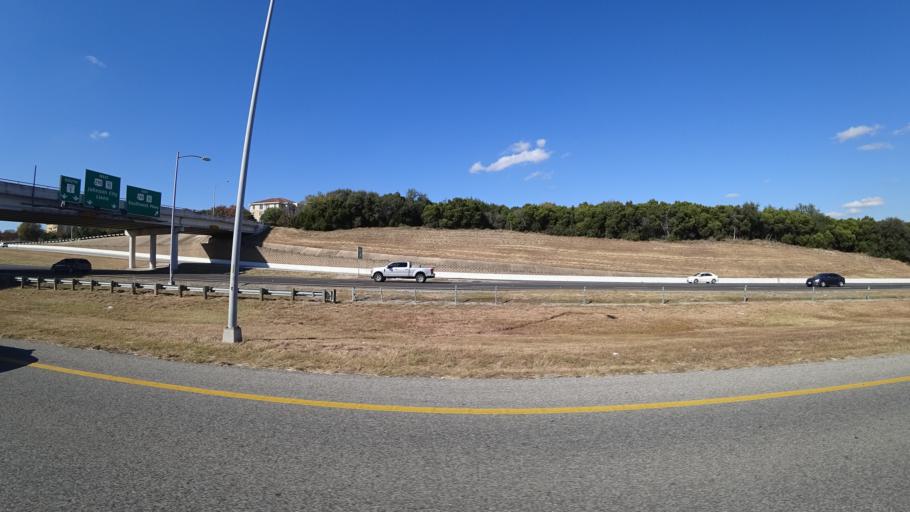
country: US
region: Texas
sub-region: Travis County
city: Rollingwood
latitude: 30.2407
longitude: -97.8150
